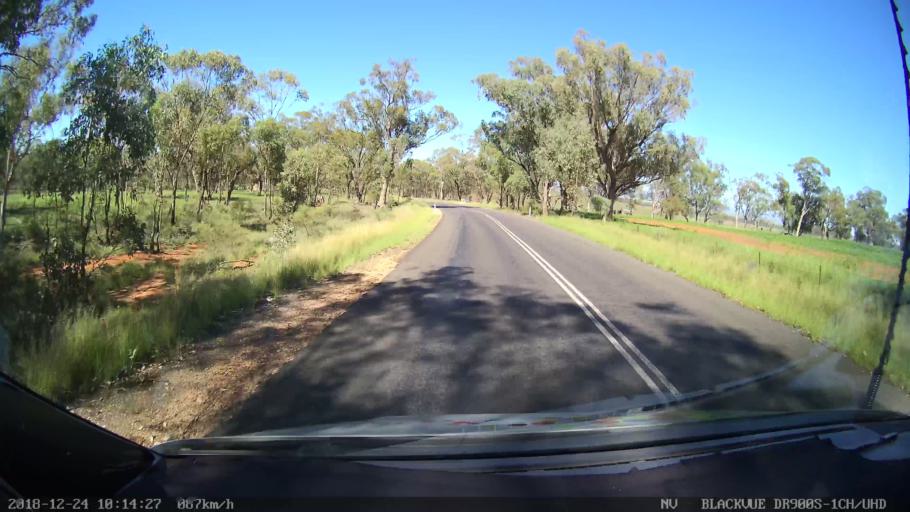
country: AU
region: New South Wales
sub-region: Liverpool Plains
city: Quirindi
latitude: -31.6976
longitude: 150.6279
